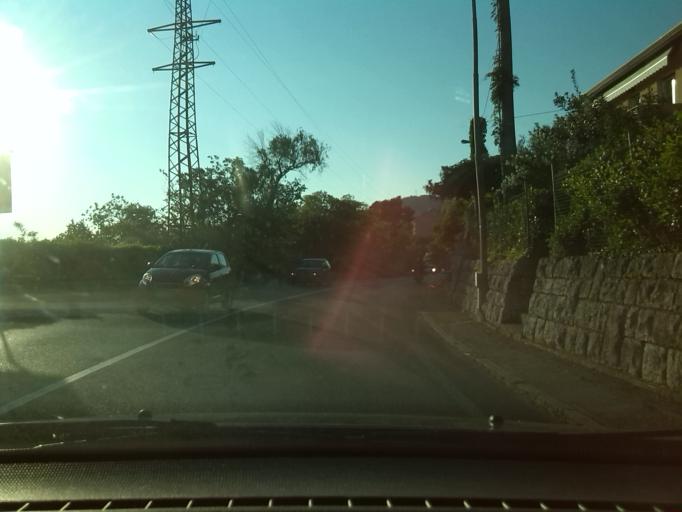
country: IT
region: Friuli Venezia Giulia
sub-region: Provincia di Trieste
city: Sistiana-Visogliano
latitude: 45.7725
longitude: 13.6354
